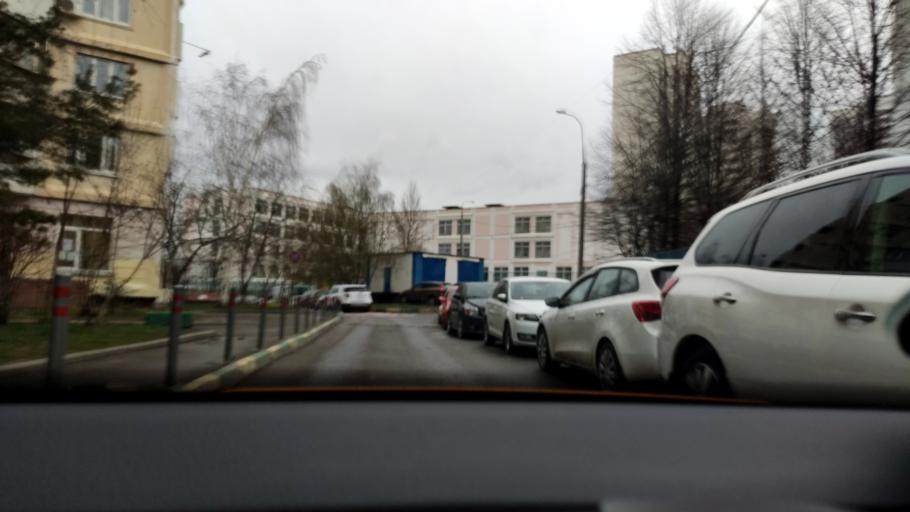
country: RU
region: Moscow
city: Strogino
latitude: 55.8425
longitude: 37.3871
